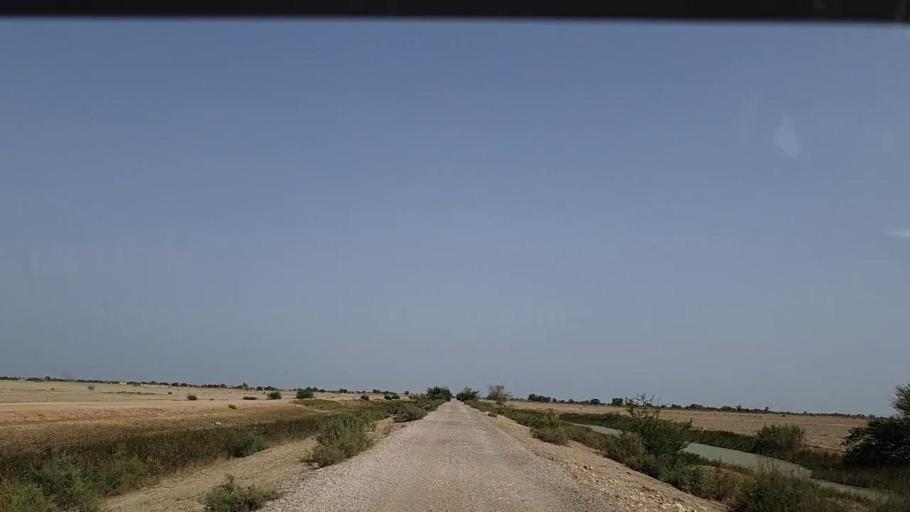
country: PK
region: Sindh
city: Johi
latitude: 26.7610
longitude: 67.6637
